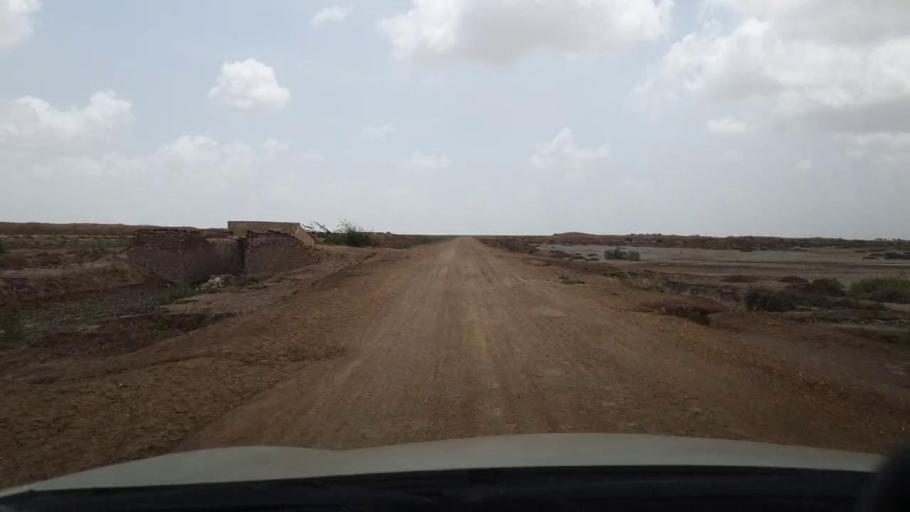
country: PK
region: Sindh
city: Kadhan
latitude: 24.3460
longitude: 68.9222
